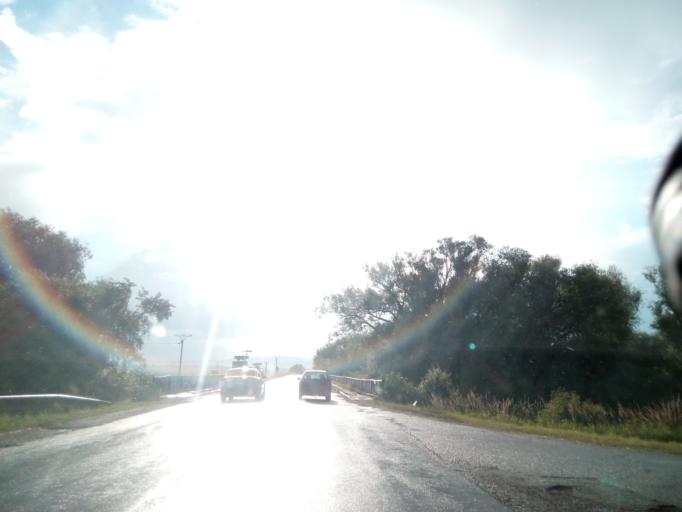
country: SK
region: Kosicky
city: Kosice
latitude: 48.6572
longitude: 21.3567
